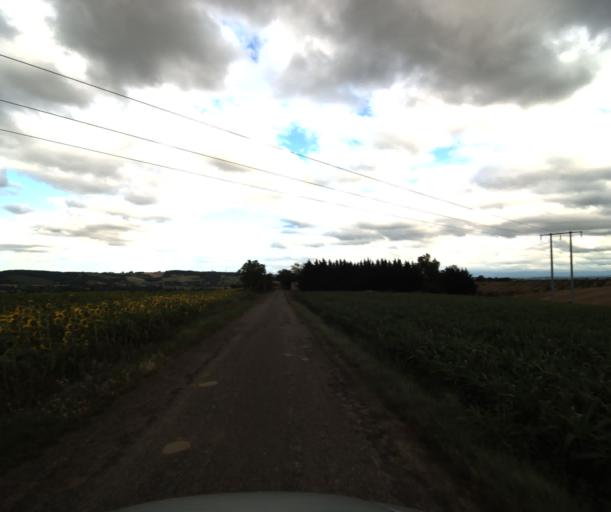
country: FR
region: Midi-Pyrenees
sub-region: Departement de la Haute-Garonne
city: Beaumont-sur-Leze
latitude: 43.3924
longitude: 1.3299
